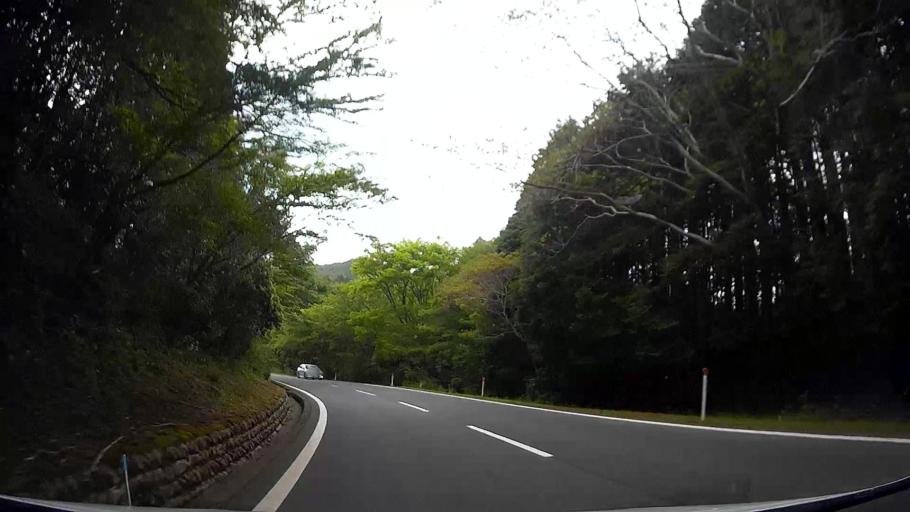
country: JP
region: Shizuoka
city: Ito
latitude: 34.9895
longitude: 139.0424
